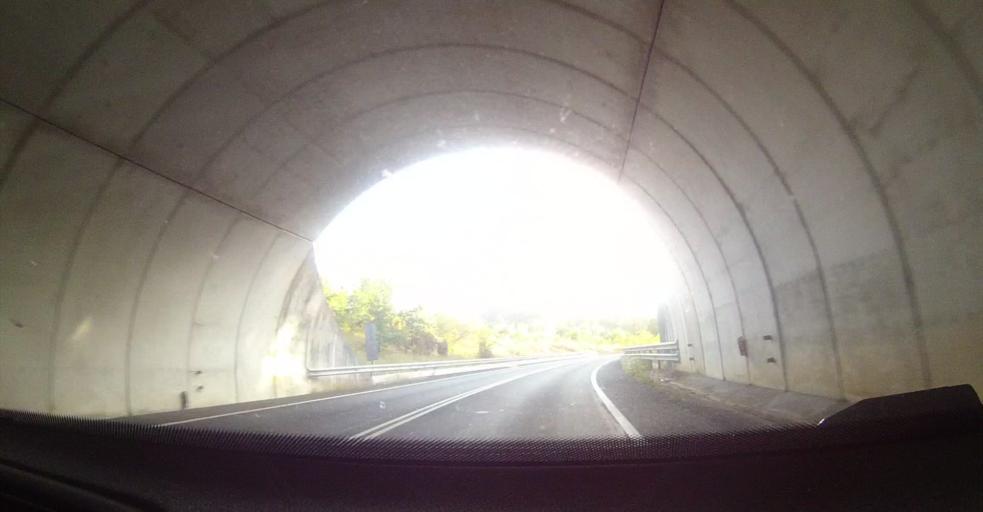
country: ES
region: Cantabria
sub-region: Provincia de Cantabria
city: Rasines
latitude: 43.3171
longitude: -3.4149
